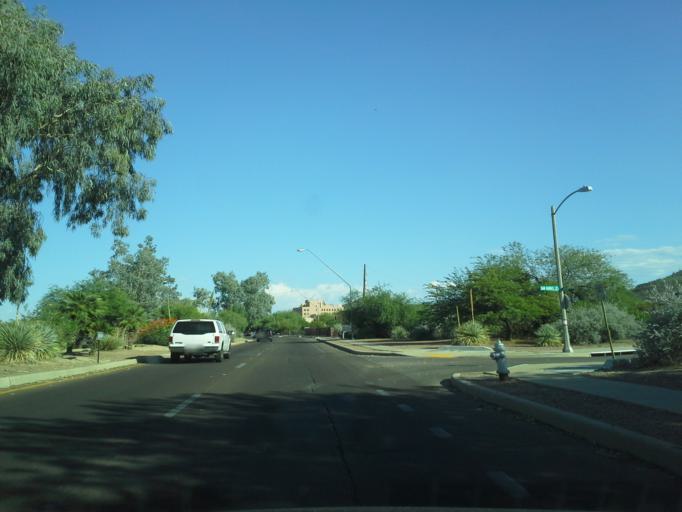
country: US
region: Arizona
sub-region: Pima County
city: South Tucson
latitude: 32.2326
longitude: -111.0024
